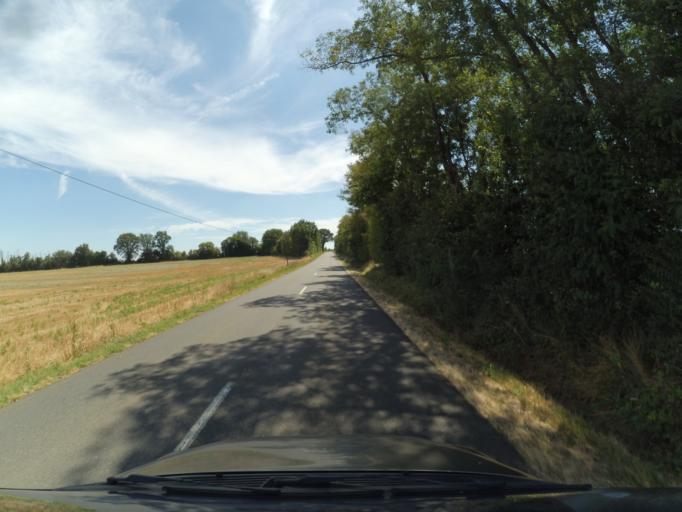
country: FR
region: Poitou-Charentes
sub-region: Departement de la Vienne
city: Usson-du-Poitou
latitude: 46.2615
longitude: 0.5221
